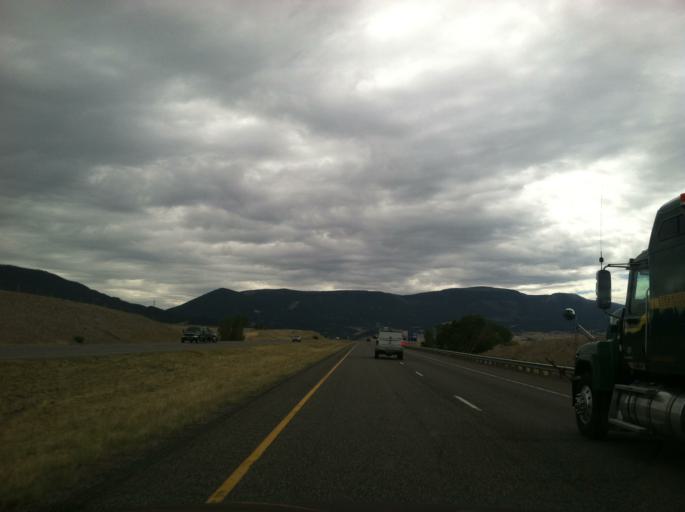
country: US
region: Montana
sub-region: Park County
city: Livingston
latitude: 45.6541
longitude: -110.5395
